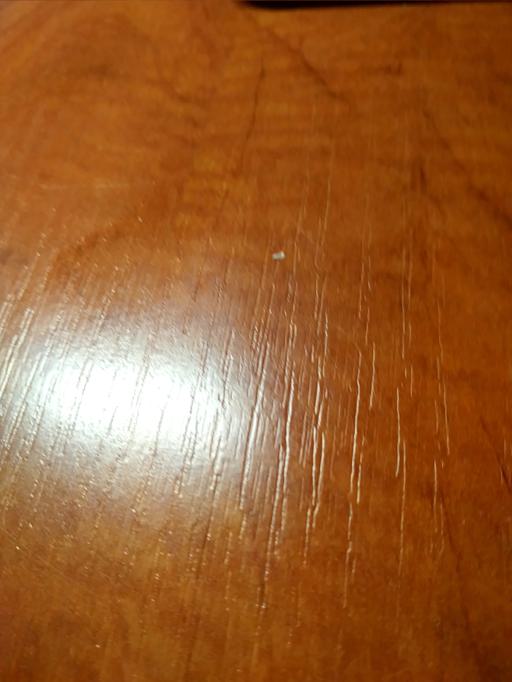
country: RU
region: Vologda
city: Khokhlovo
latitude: 59.4512
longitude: 37.3335
